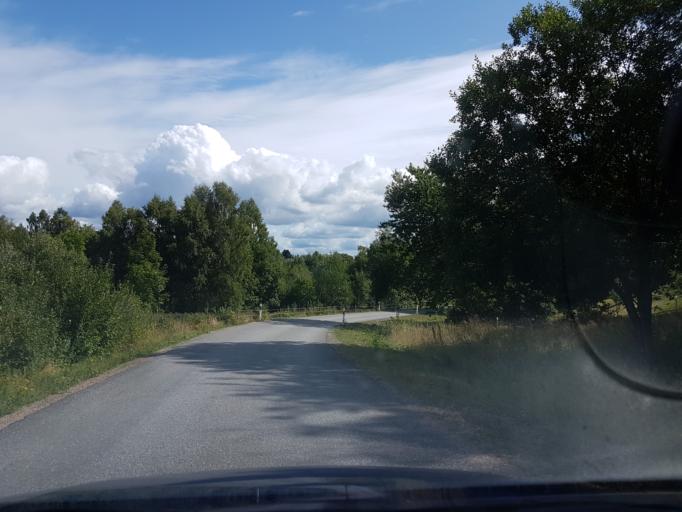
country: SE
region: Vaestra Goetaland
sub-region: Lerums Kommun
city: Grabo
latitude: 57.8465
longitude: 12.3166
